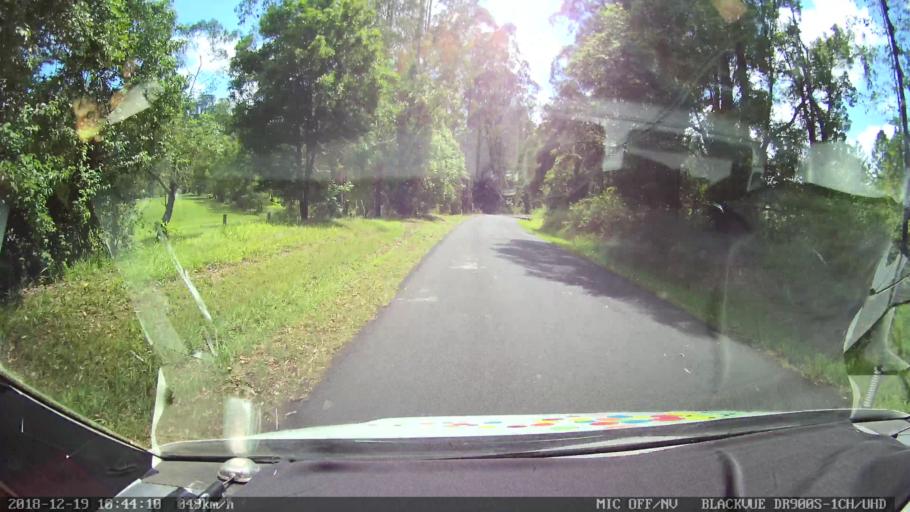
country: AU
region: New South Wales
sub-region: Lismore Municipality
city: Nimbin
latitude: -28.5962
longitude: 153.1785
